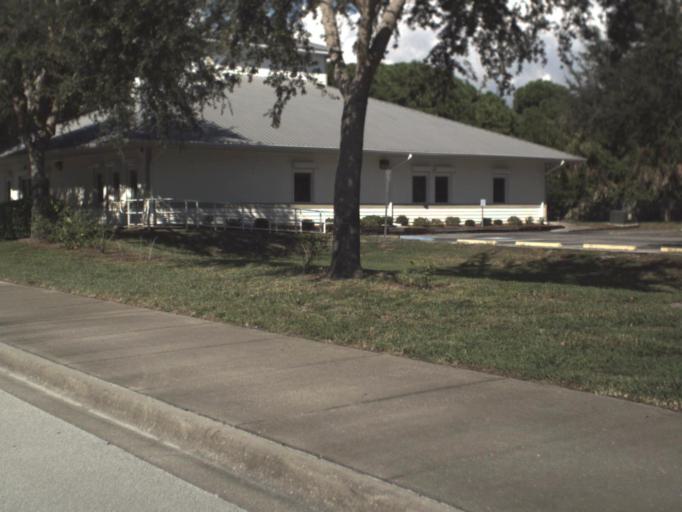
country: US
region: Florida
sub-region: Sarasota County
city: Englewood
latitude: 26.9502
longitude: -82.3531
